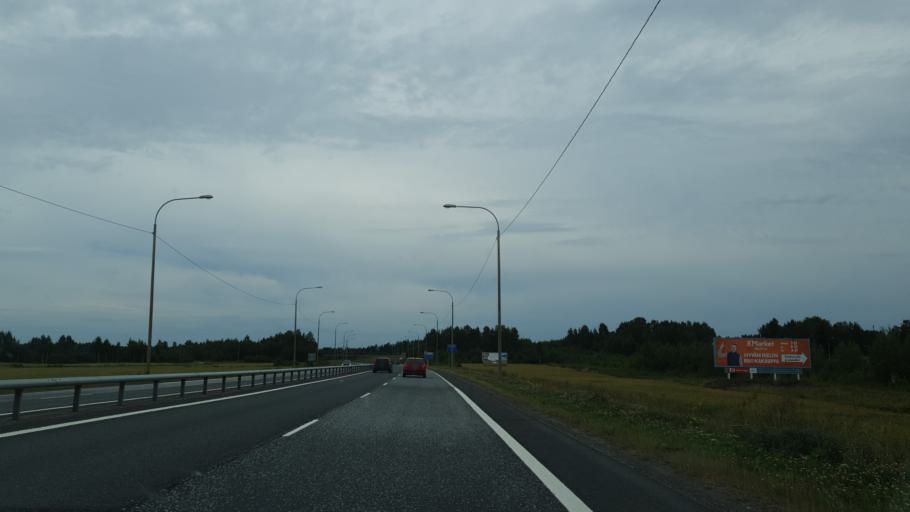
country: FI
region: North Karelia
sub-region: Joensuu
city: Joensuu
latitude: 62.5509
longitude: 29.8407
